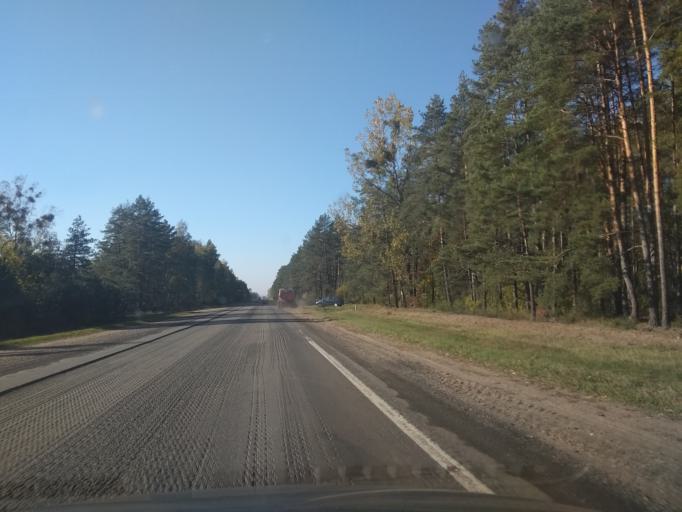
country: BY
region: Grodnenskaya
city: Zhyrovichy
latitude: 53.0605
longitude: 25.4288
